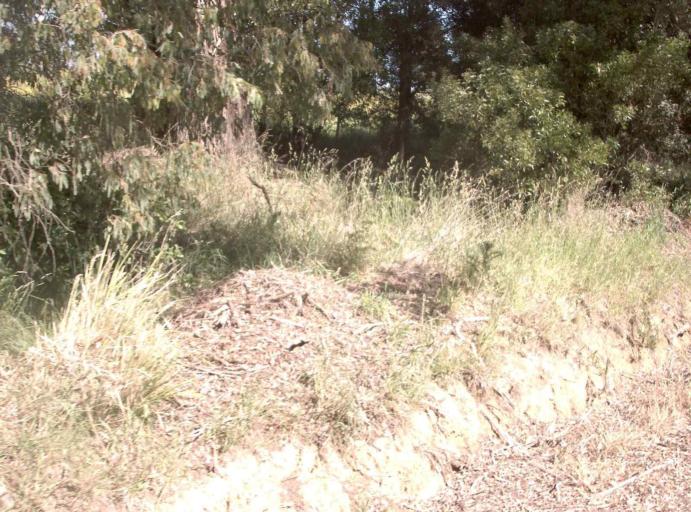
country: AU
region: New South Wales
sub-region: Bombala
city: Bombala
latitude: -37.1774
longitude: 148.7251
